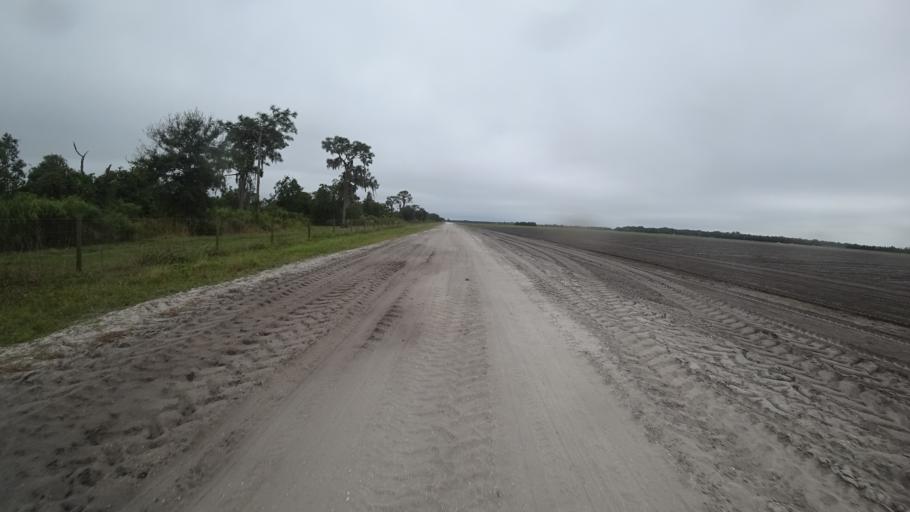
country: US
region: Florida
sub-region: Sarasota County
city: Warm Mineral Springs
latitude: 27.2922
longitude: -82.1346
